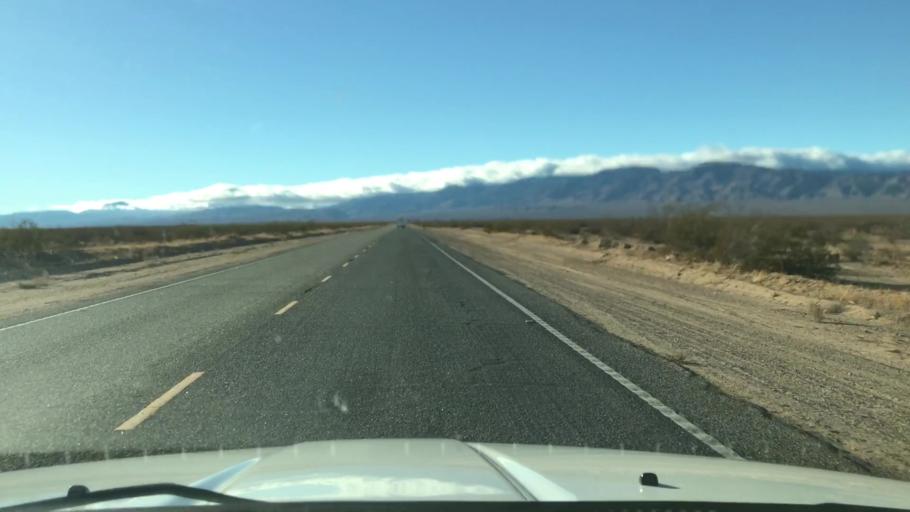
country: US
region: California
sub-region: Kern County
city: California City
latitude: 35.1256
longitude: -118.0418
